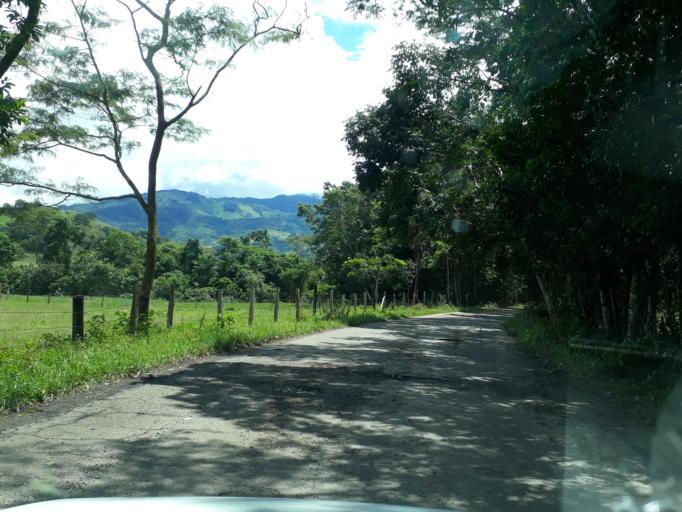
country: CO
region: Cundinamarca
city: Medina
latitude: 4.5789
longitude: -73.3301
